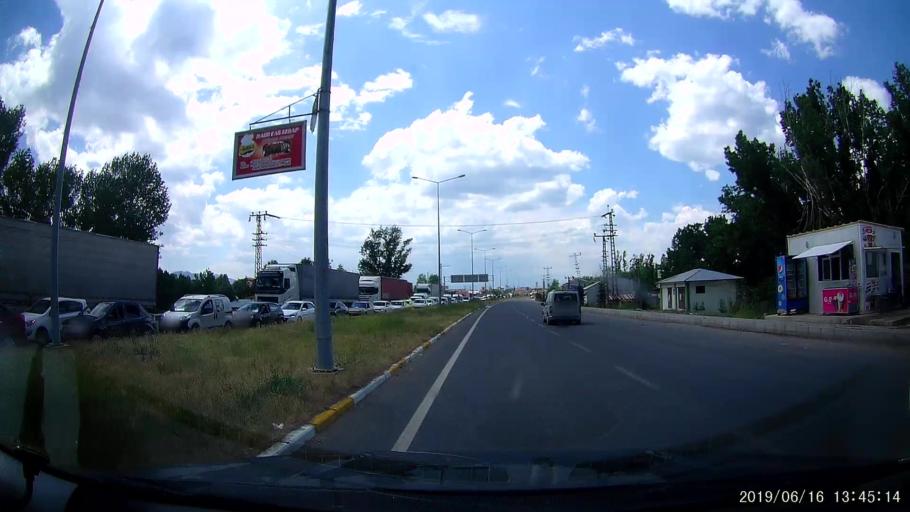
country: TR
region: Agri
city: Agri
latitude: 39.7083
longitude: 43.0482
